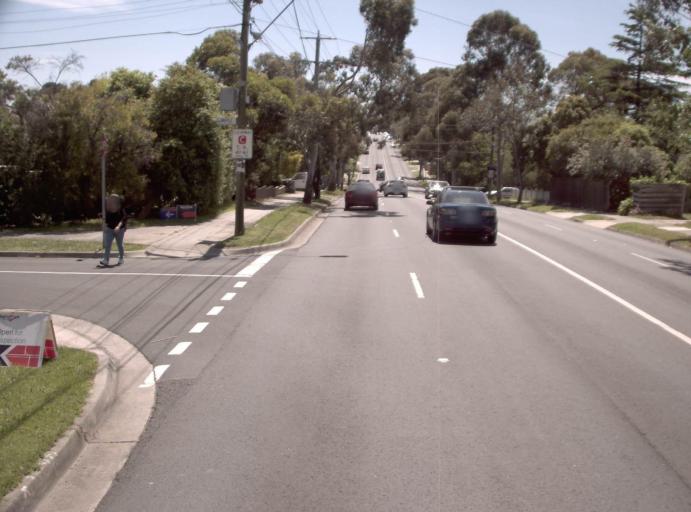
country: AU
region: Victoria
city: Burwood East
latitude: -37.8698
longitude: 145.1488
